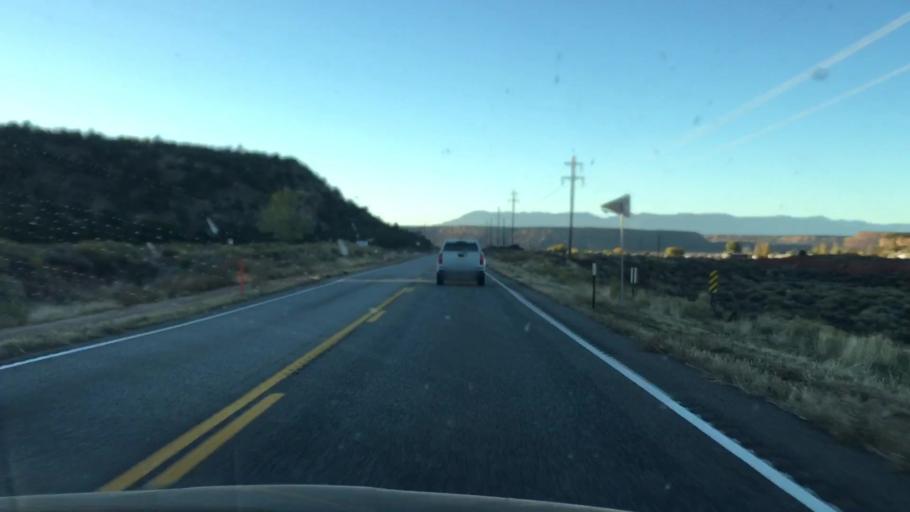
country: US
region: Arizona
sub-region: Mohave County
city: Colorado City
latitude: 37.0944
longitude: -113.1186
